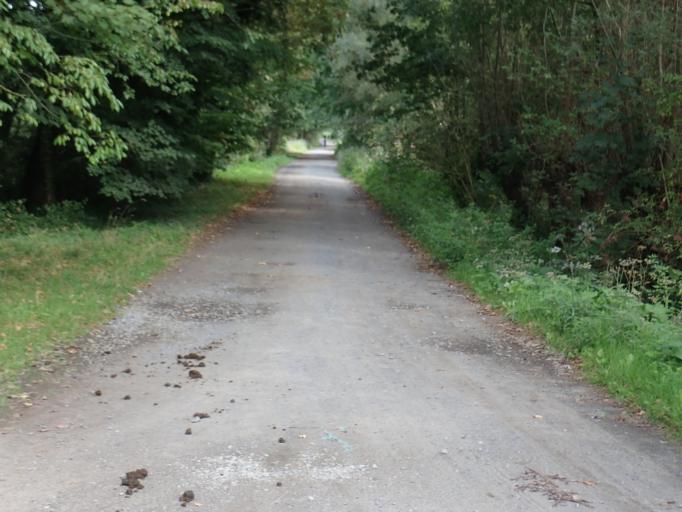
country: BE
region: Flanders
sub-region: Provincie Antwerpen
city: Sint-Amands
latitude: 51.0670
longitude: 4.2083
